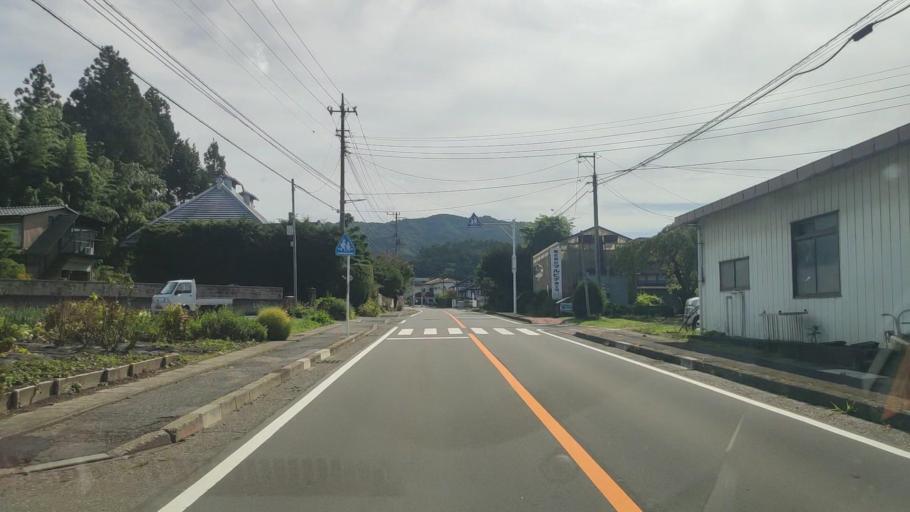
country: JP
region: Gunma
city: Numata
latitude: 36.6280
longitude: 138.9636
